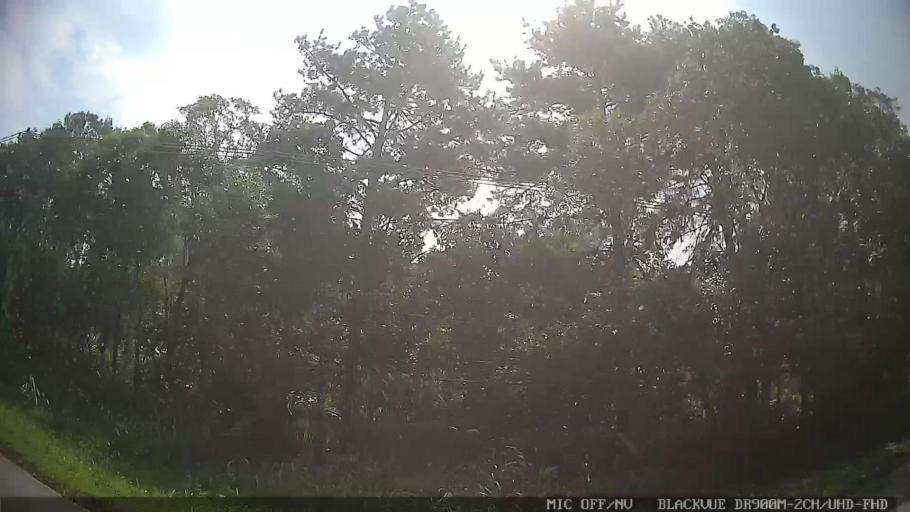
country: BR
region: Sao Paulo
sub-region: Ribeirao Pires
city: Ribeirao Pires
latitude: -23.6653
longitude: -46.3804
